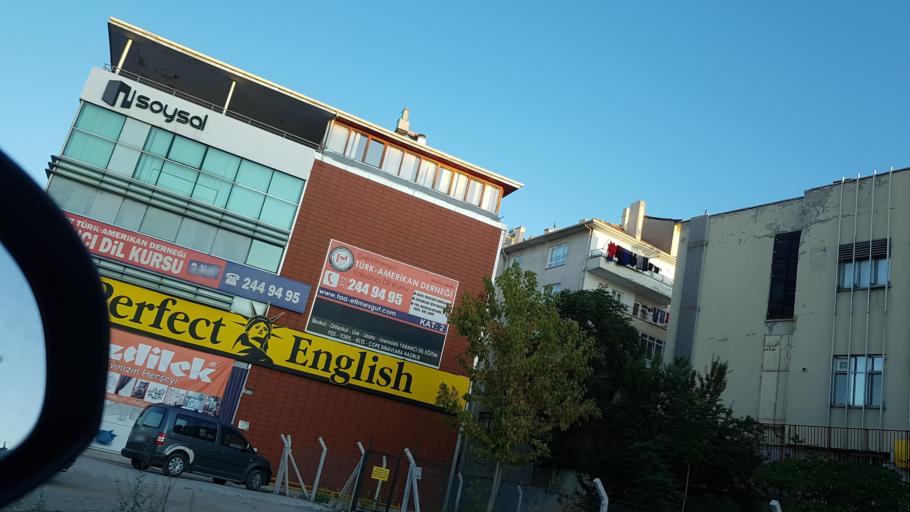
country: TR
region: Ankara
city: Etimesgut
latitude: 39.9475
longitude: 32.6691
